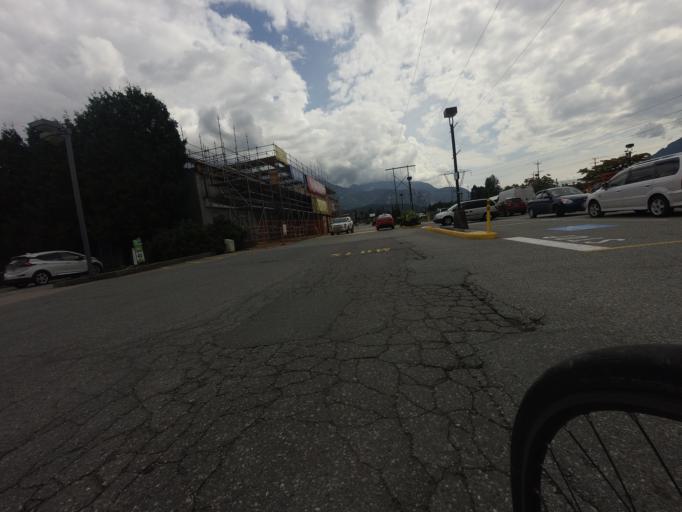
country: CA
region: British Columbia
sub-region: Greater Vancouver Regional District
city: Lions Bay
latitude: 49.7404
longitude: -123.1339
